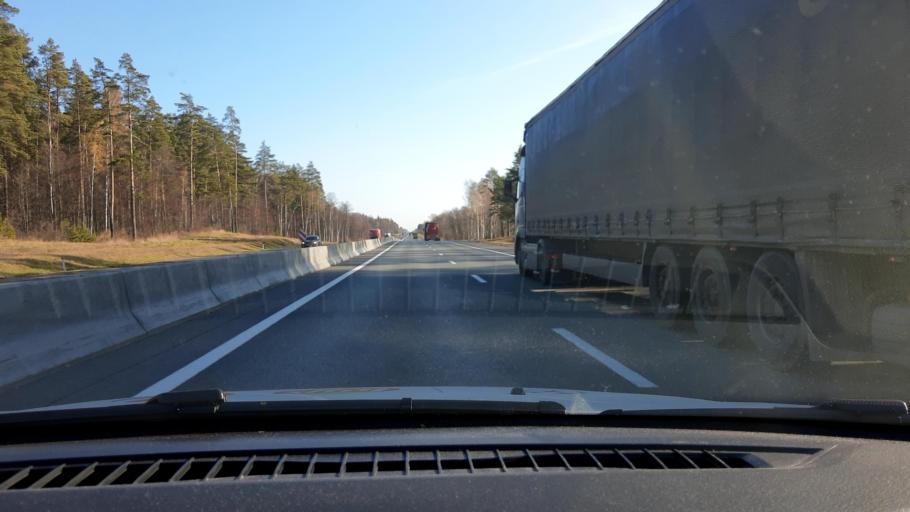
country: RU
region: Nizjnij Novgorod
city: Yuganets
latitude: 56.2878
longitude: 43.2298
